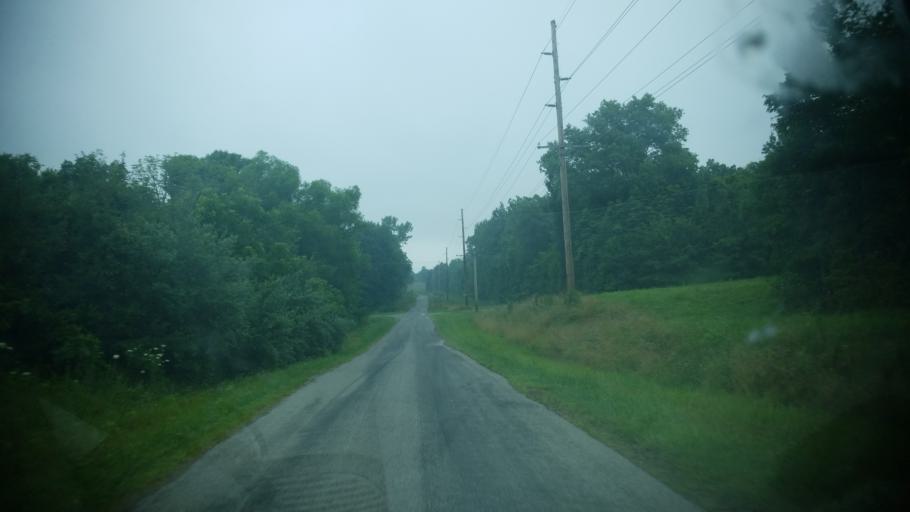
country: US
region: Illinois
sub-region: Clay County
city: Flora
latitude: 38.5580
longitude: -88.4019
